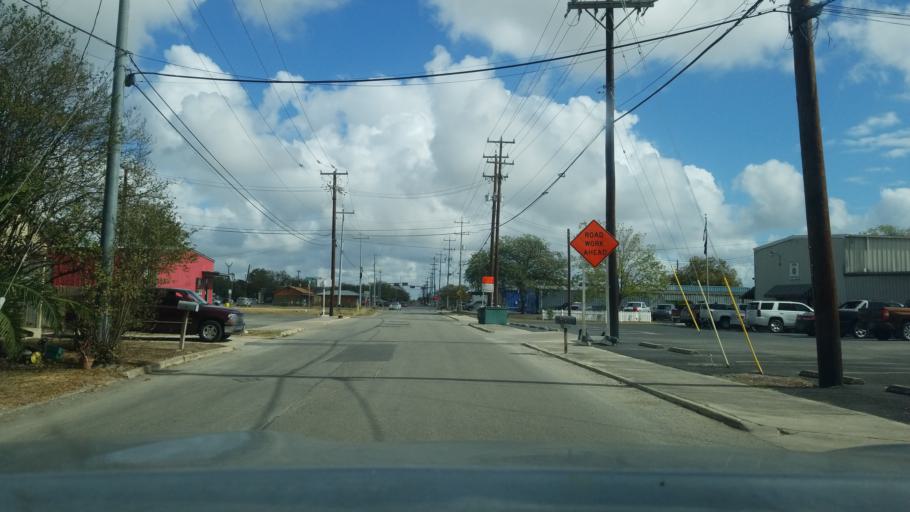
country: US
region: Texas
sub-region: Bexar County
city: Universal City
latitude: 29.5440
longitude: -98.2902
